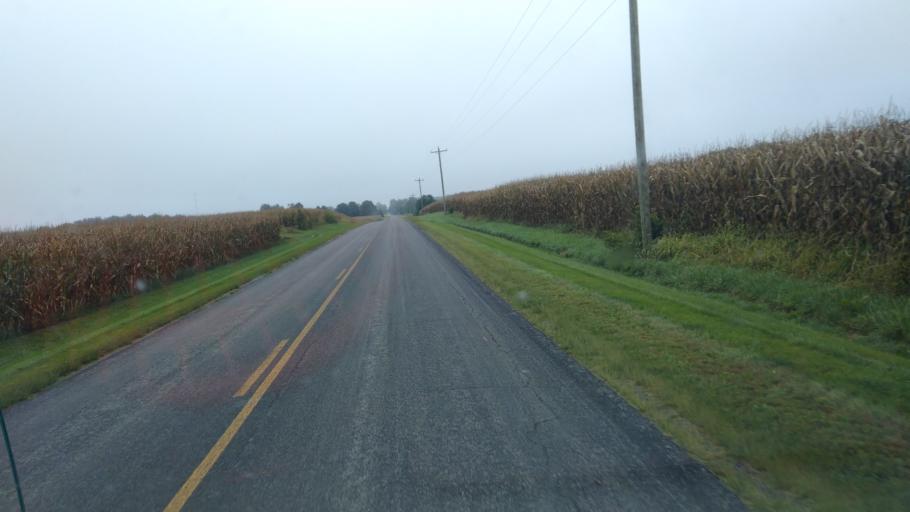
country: US
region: Ohio
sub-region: Union County
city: Richwood
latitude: 40.4922
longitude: -83.3799
